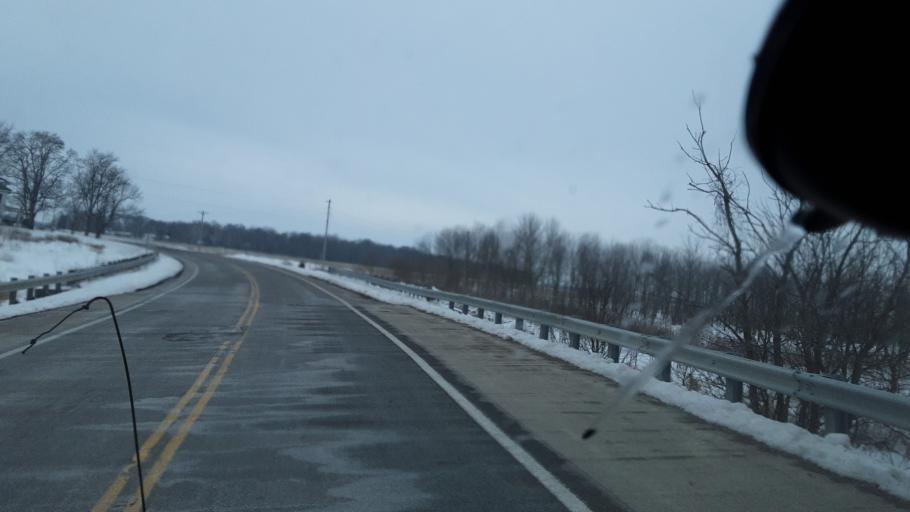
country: US
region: Ohio
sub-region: Champaign County
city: Mechanicsburg
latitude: 40.1219
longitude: -83.4558
